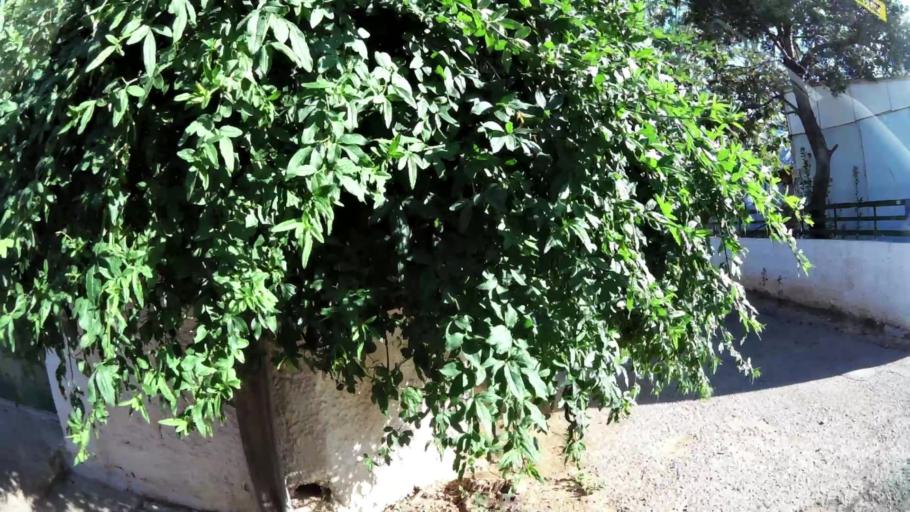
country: GR
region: Attica
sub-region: Nomarchia Anatolikis Attikis
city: Acharnes
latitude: 38.0971
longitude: 23.7200
